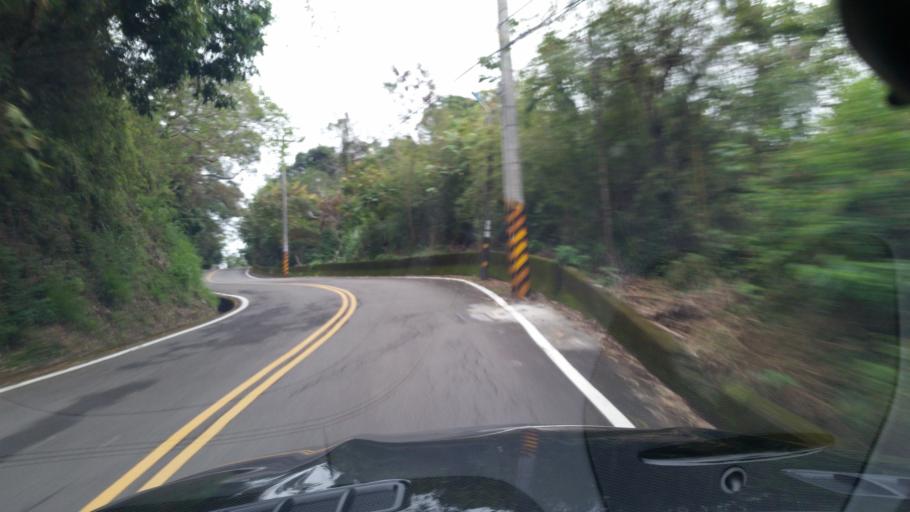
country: TW
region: Taiwan
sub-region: Miaoli
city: Miaoli
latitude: 24.5821
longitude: 120.8802
